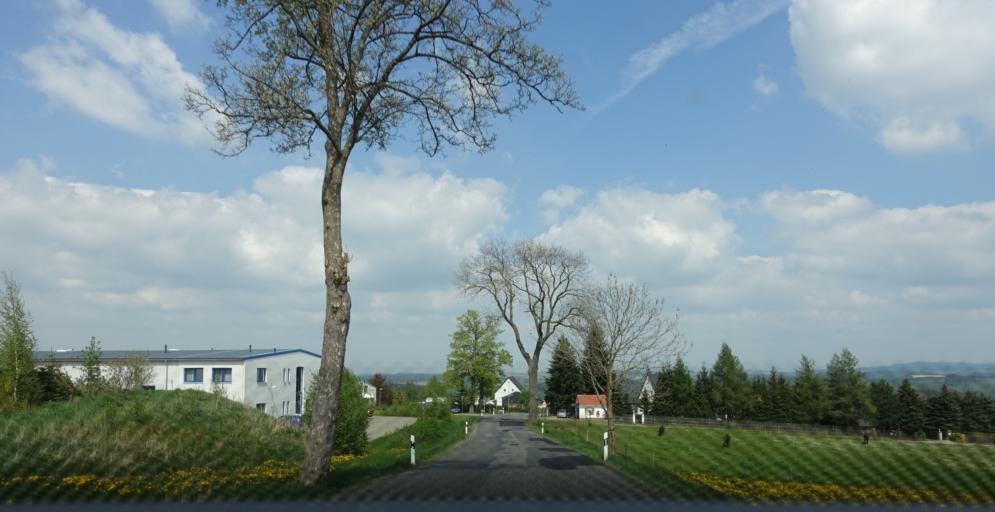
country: DE
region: Saxony
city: Lengefeld
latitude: 50.7158
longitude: 13.1848
